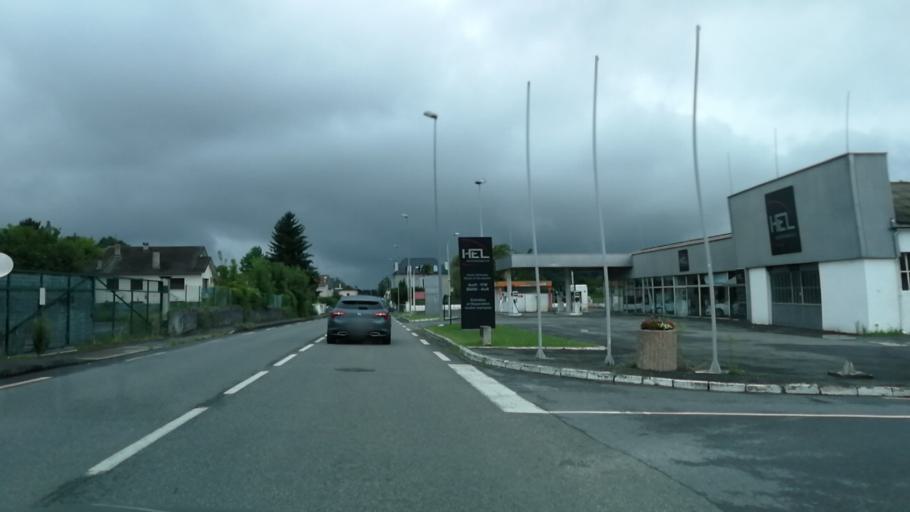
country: FR
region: Aquitaine
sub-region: Departement des Pyrenees-Atlantiques
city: Oloron-Sainte-Marie
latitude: 43.1734
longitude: -0.6043
